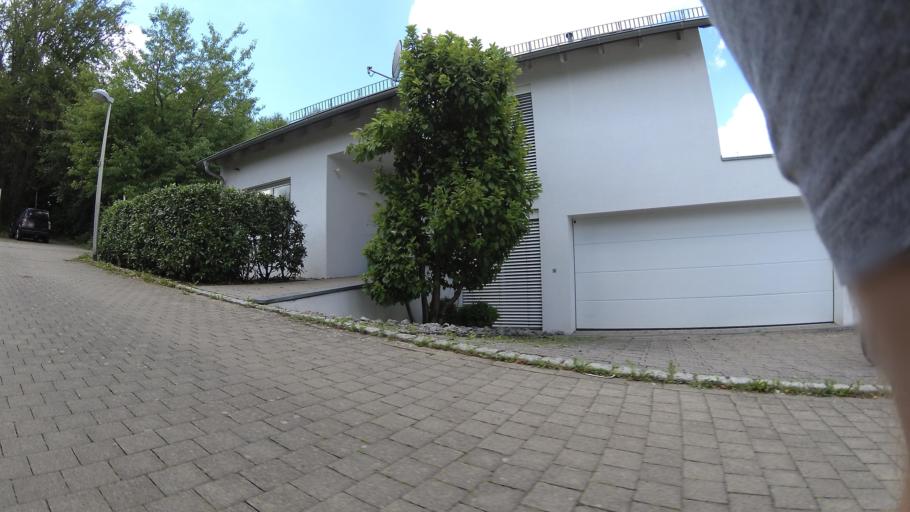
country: DE
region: Baden-Wuerttemberg
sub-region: Regierungsbezirk Stuttgart
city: Heilbronn
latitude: 49.1386
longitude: 9.2431
